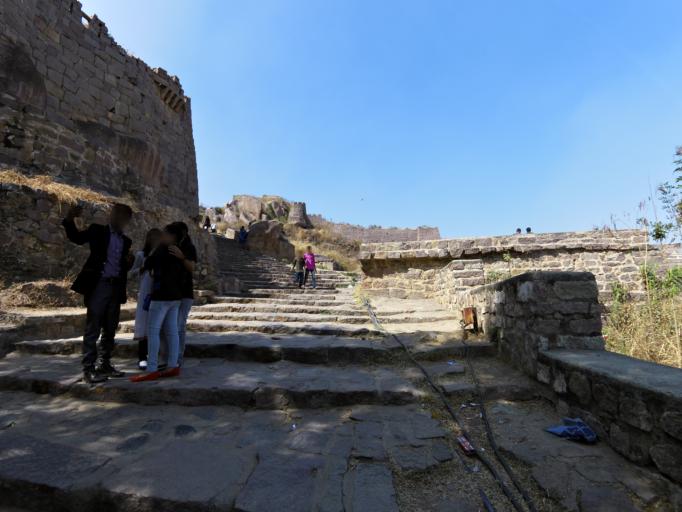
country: IN
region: Telangana
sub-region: Hyderabad
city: Hyderabad
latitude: 17.3852
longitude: 78.4013
